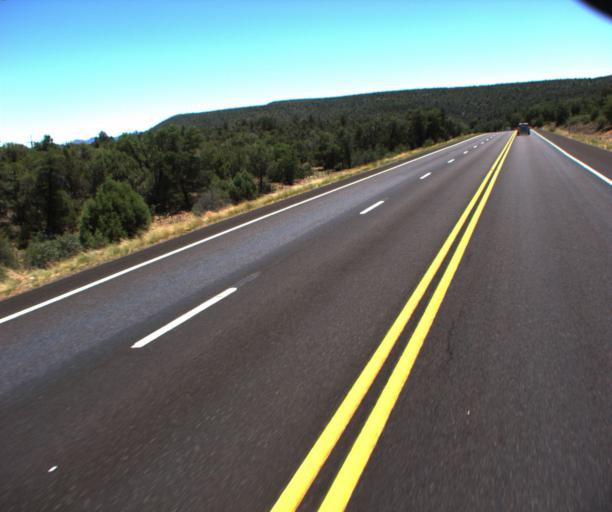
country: US
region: Arizona
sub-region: Gila County
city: Pine
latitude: 34.3261
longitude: -111.4179
